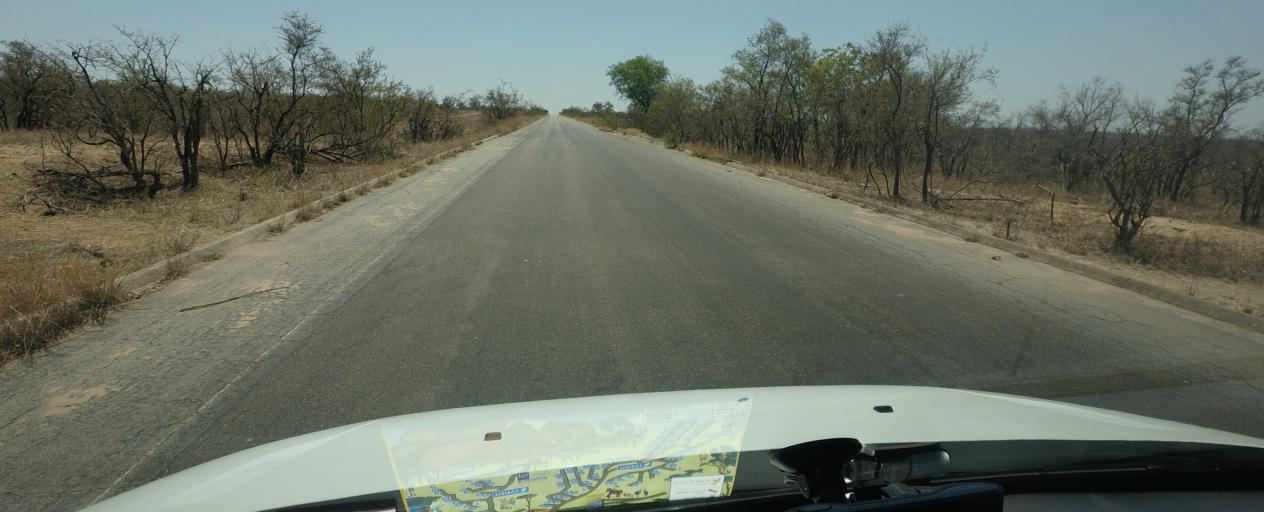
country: ZA
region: Limpopo
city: Thulamahashi
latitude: -24.5355
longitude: 31.3753
